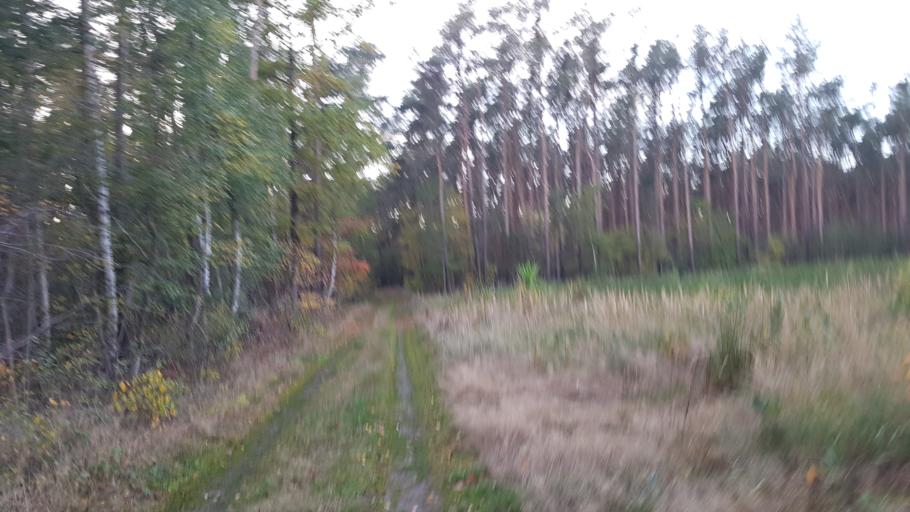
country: DE
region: Brandenburg
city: Bad Liebenwerda
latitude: 51.5418
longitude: 13.4336
